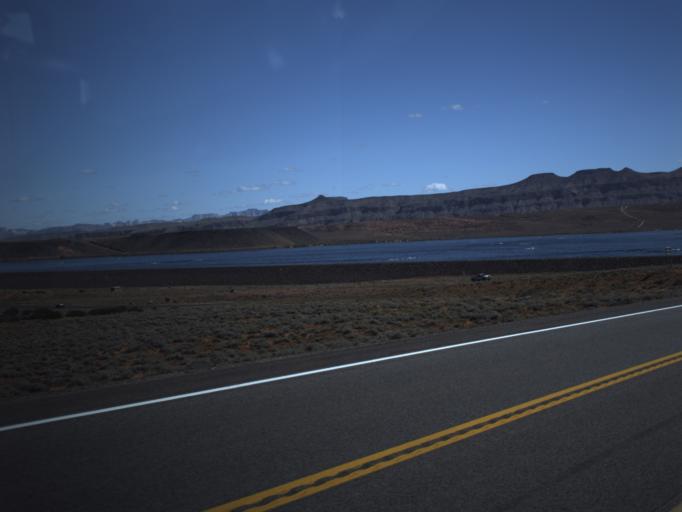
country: US
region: Utah
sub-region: Washington County
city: Washington
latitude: 37.1078
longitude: -113.3985
